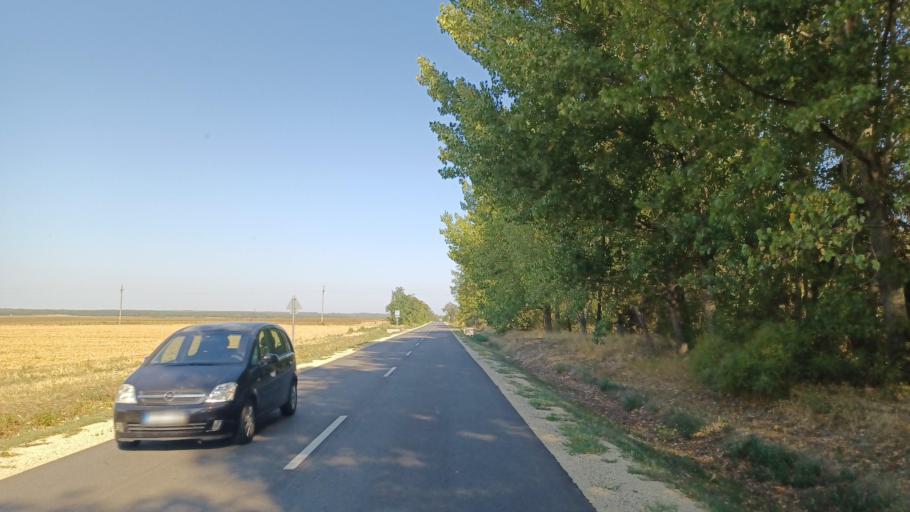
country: HU
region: Tolna
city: Paks
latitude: 46.6561
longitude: 18.8345
